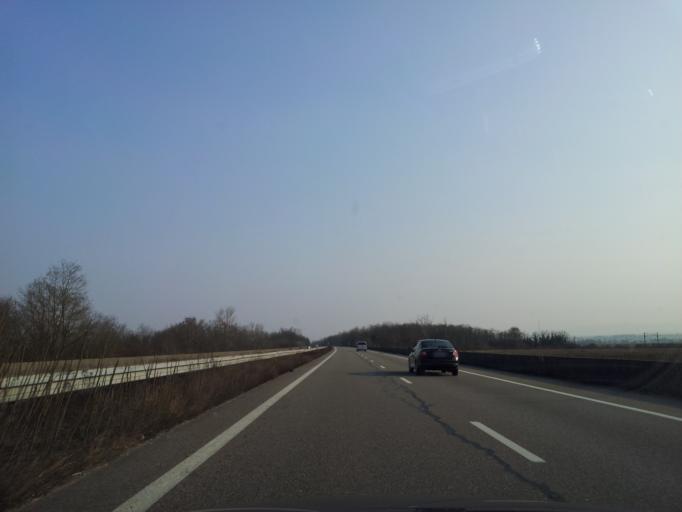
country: FR
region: Alsace
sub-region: Departement du Haut-Rhin
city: Blotzheim
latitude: 47.6272
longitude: 7.5065
